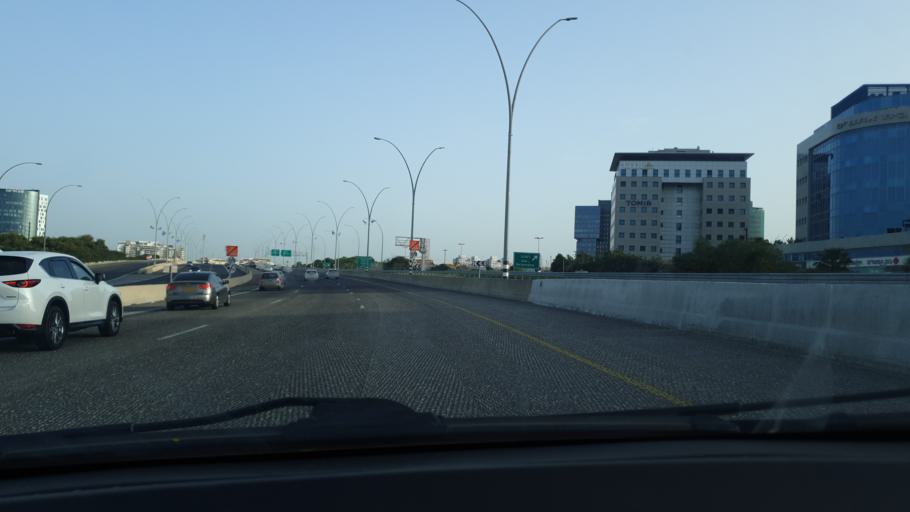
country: IL
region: Central District
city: Ra'anana
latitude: 32.1974
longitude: 34.8851
